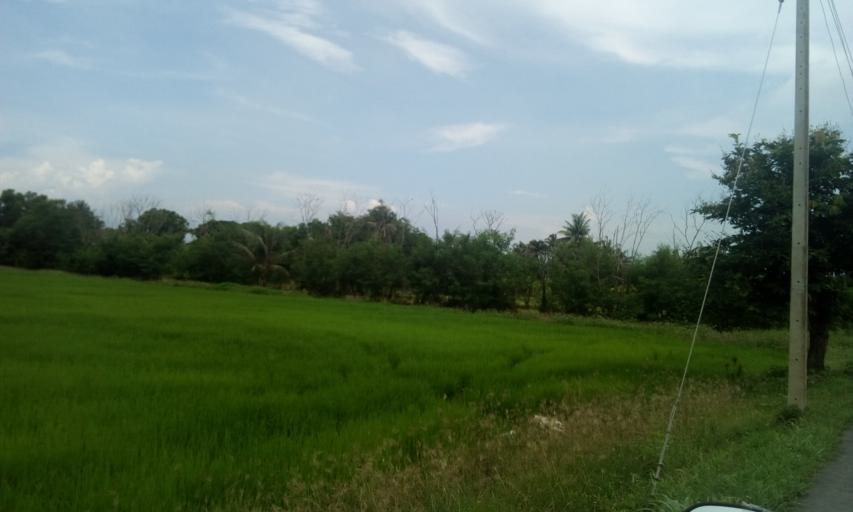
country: TH
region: Pathum Thani
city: Ban Lam Luk Ka
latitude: 14.0183
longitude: 100.8434
